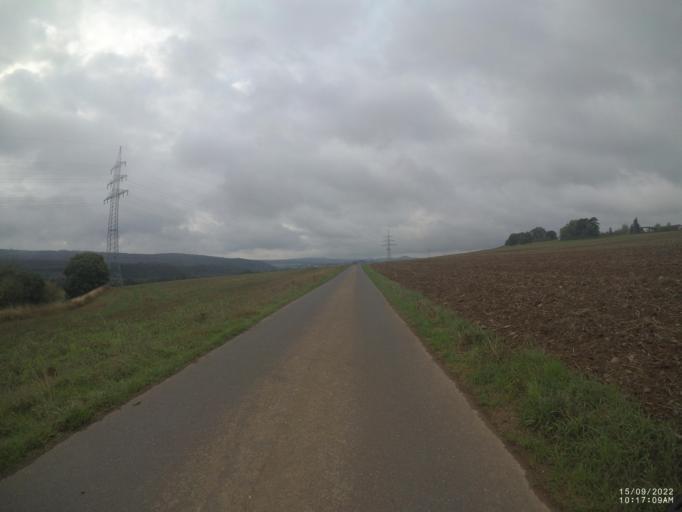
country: DE
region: Rheinland-Pfalz
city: Trierscheid
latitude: 50.3516
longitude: 6.7979
